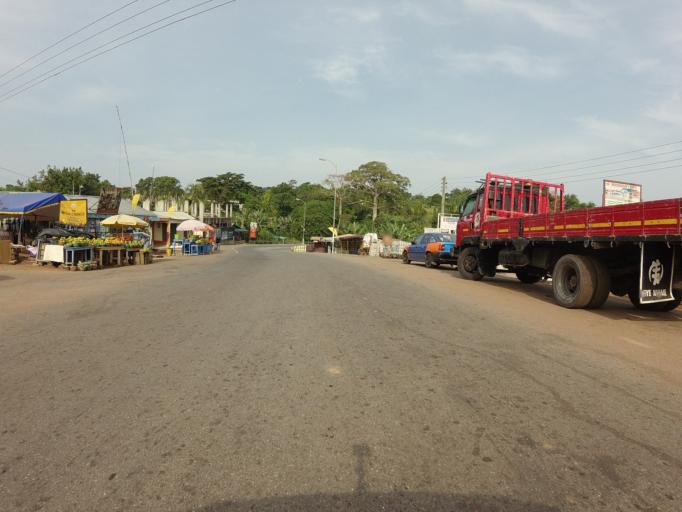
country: GH
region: Eastern
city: Aburi
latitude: 5.8141
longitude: -0.1868
